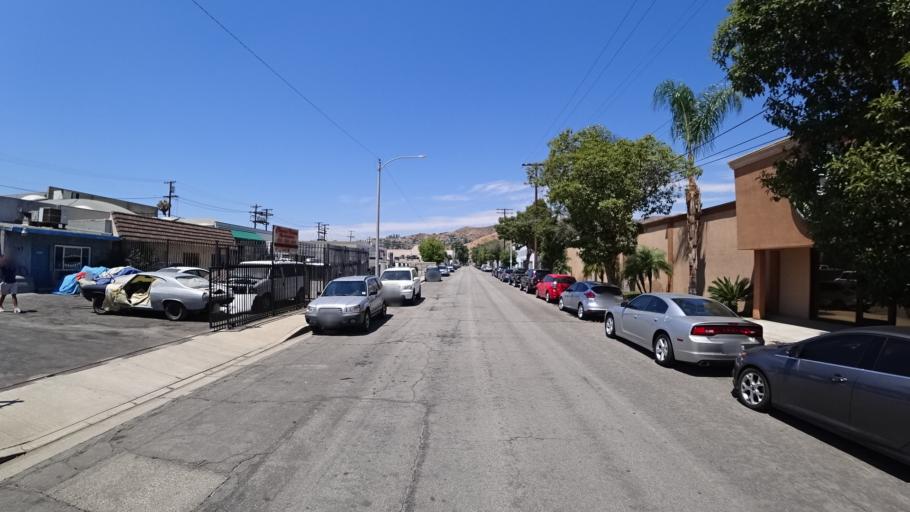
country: US
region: California
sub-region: Los Angeles County
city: Burbank
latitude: 34.2046
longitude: -118.3455
